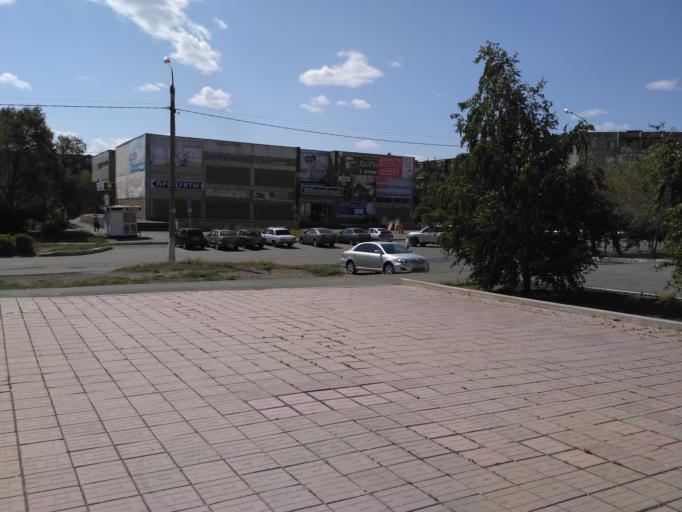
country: RU
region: Orenburg
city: Novotroitsk
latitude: 51.1884
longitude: 58.2847
